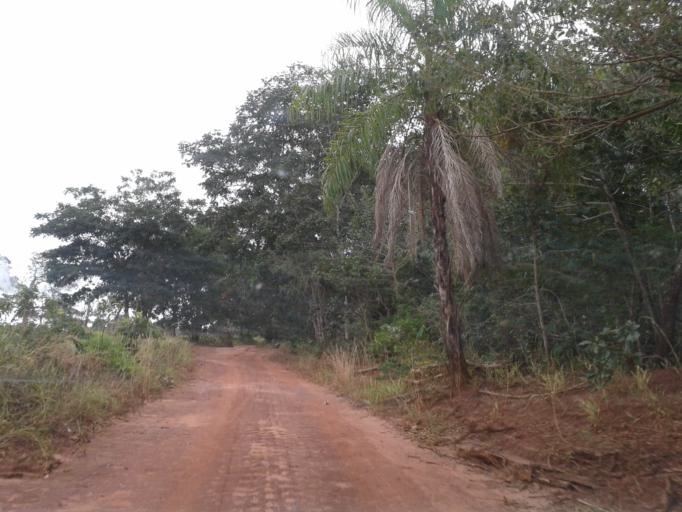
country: BR
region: Minas Gerais
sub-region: Campina Verde
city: Campina Verde
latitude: -19.5098
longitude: -49.6618
